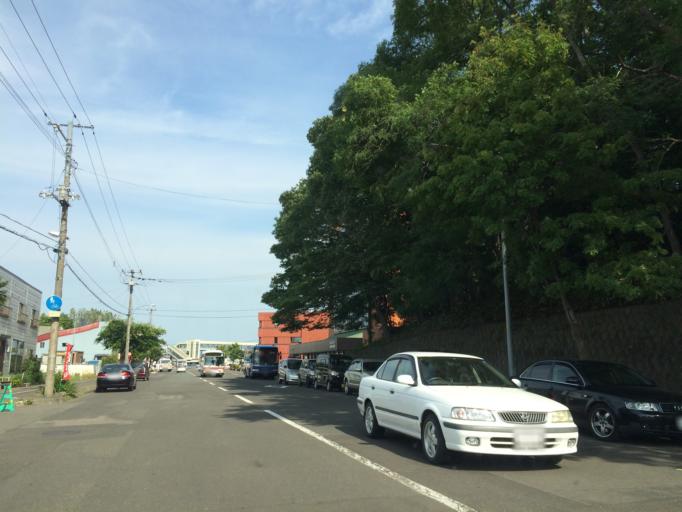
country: JP
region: Hokkaido
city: Ebetsu
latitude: 43.1112
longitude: 141.5540
